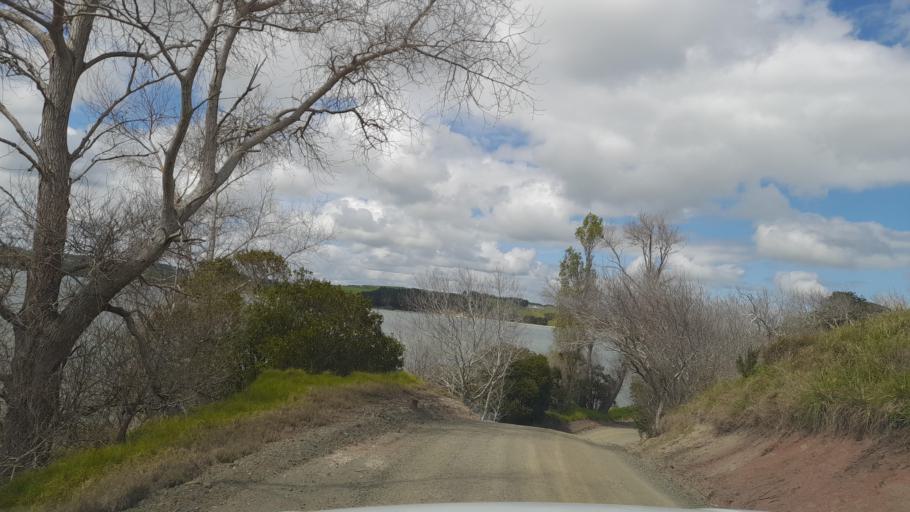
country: NZ
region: Auckland
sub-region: Auckland
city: Wellsford
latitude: -36.2188
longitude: 174.3210
